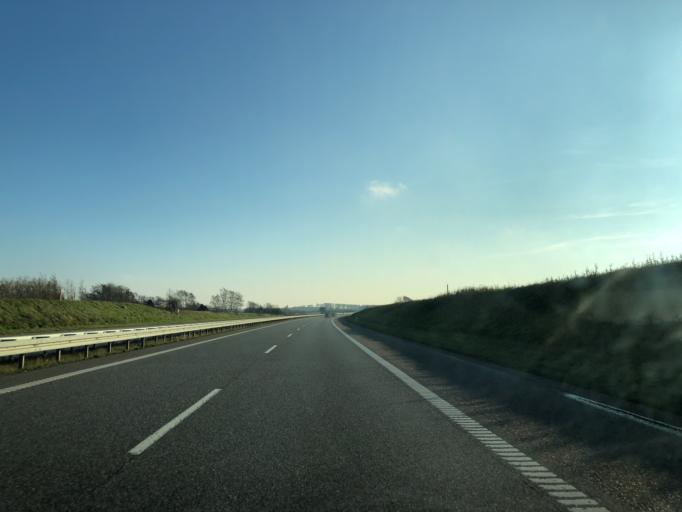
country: DK
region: South Denmark
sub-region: Vejle Kommune
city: Vejle
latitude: 55.7567
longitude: 9.5739
